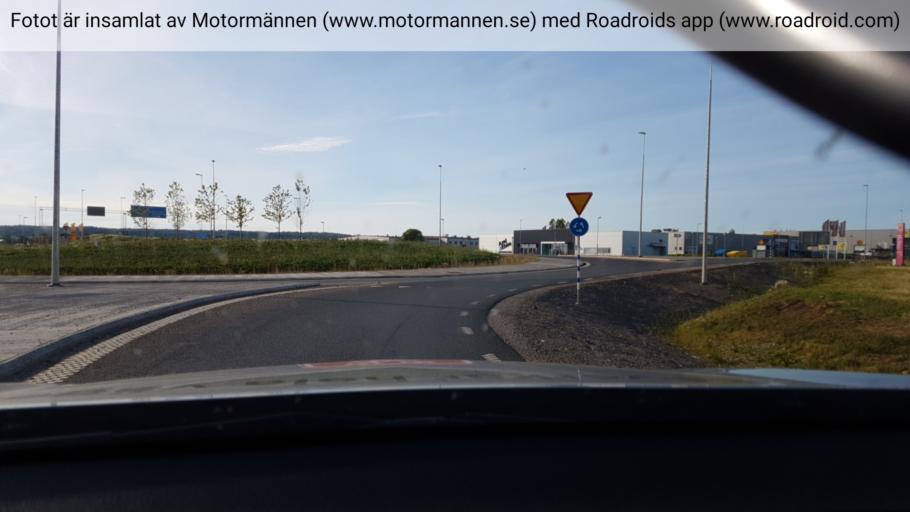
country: SE
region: Vaestra Goetaland
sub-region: Falkopings Kommun
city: Falkoeping
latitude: 58.1487
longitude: 13.5623
